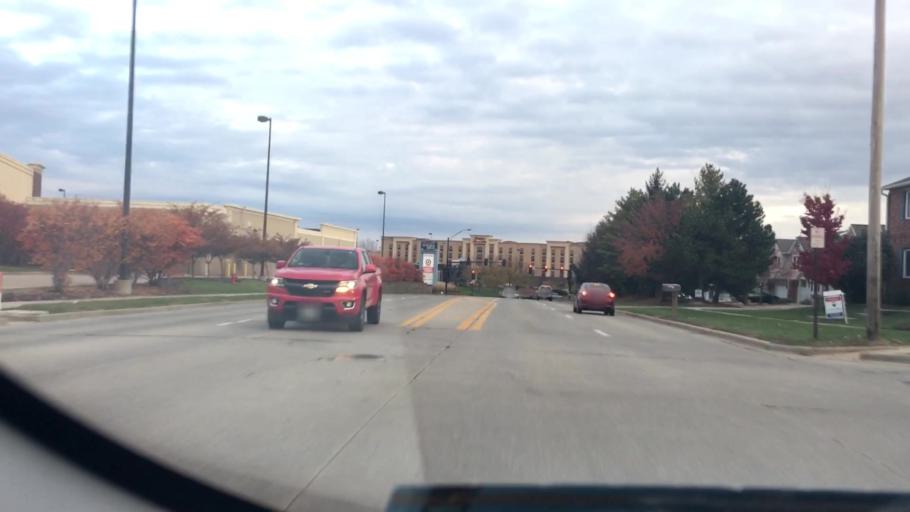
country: US
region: Illinois
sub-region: McLean County
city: Normal
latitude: 40.5063
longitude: -88.9589
